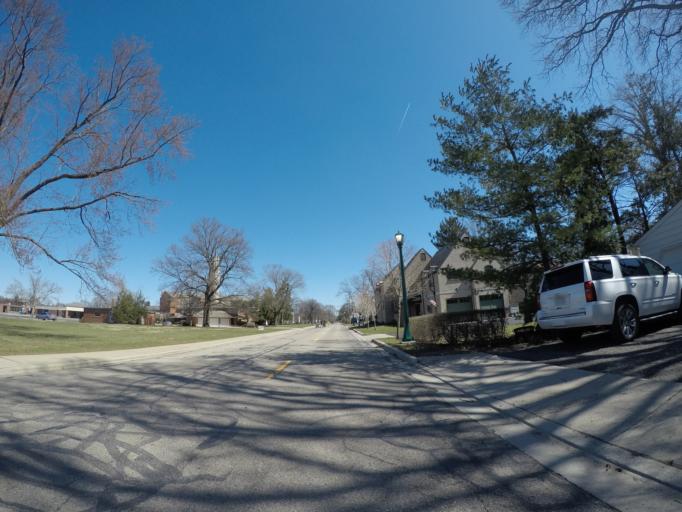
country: US
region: Ohio
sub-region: Franklin County
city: Upper Arlington
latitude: 40.0120
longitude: -83.0625
